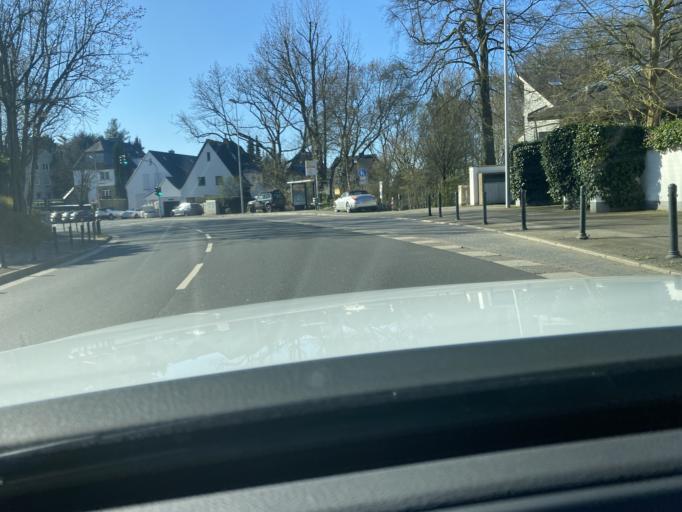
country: DE
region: North Rhine-Westphalia
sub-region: Regierungsbezirk Dusseldorf
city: Ratingen
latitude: 51.2491
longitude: 6.8602
